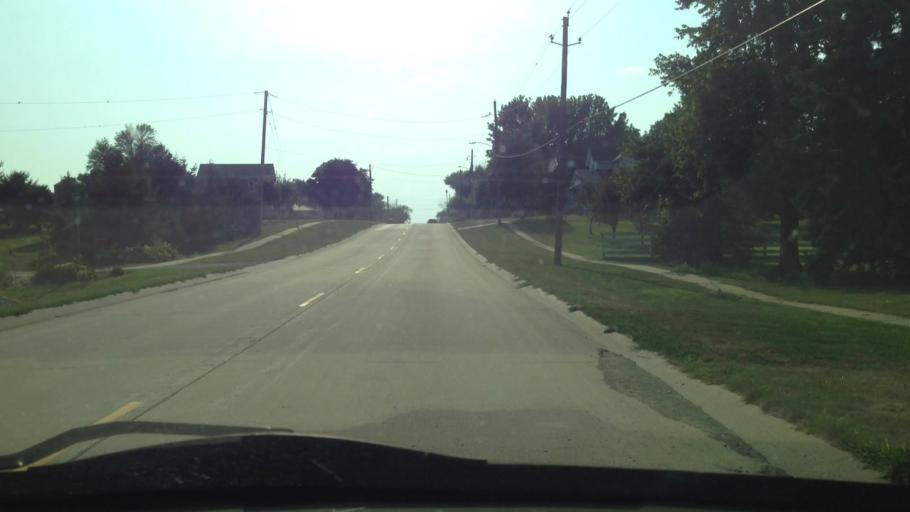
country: US
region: Iowa
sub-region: Henry County
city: Winfield
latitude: 41.2140
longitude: -91.5338
